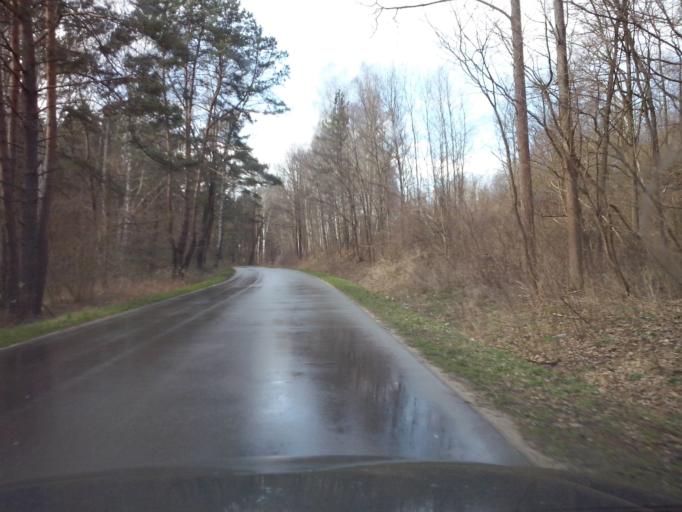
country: PL
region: Subcarpathian Voivodeship
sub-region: Powiat nizanski
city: Bieliny
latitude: 50.4320
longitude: 22.3077
